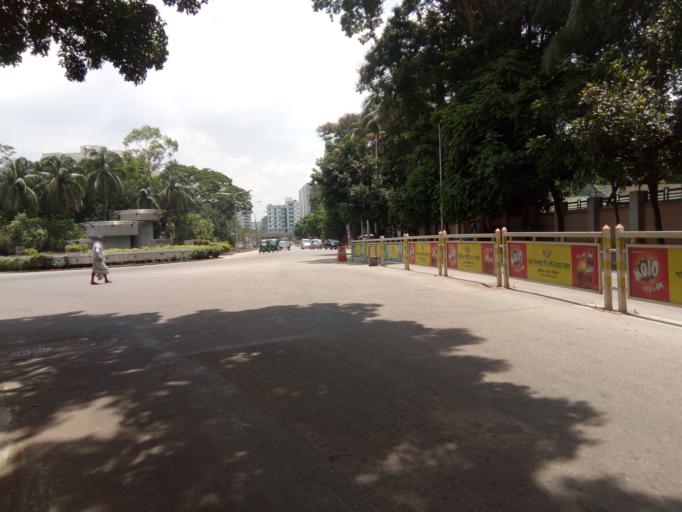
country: BD
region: Dhaka
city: Paltan
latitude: 23.7423
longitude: 90.3991
